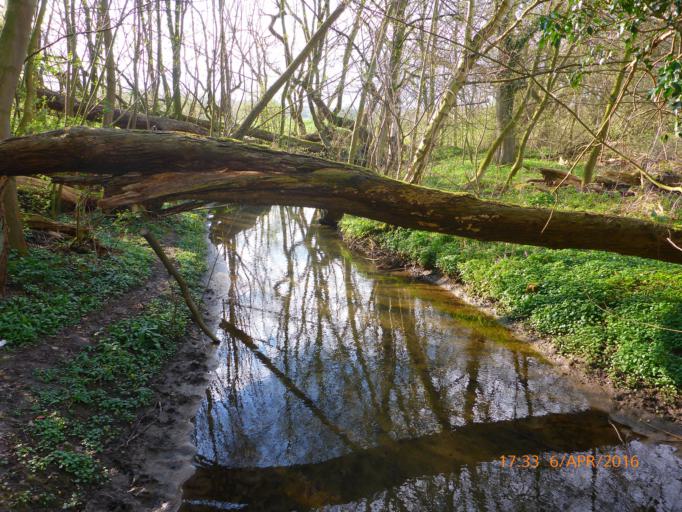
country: DE
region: Lower Saxony
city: Lauenau
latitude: 52.2759
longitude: 9.3655
